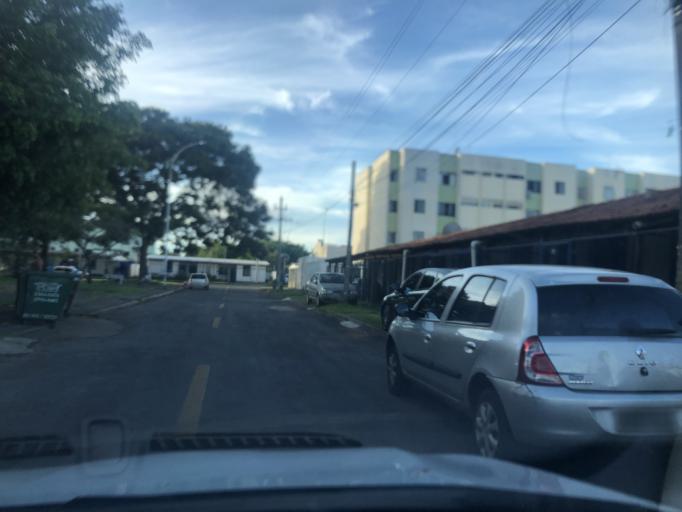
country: BR
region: Federal District
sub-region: Brasilia
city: Brasilia
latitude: -15.8229
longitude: -47.9860
